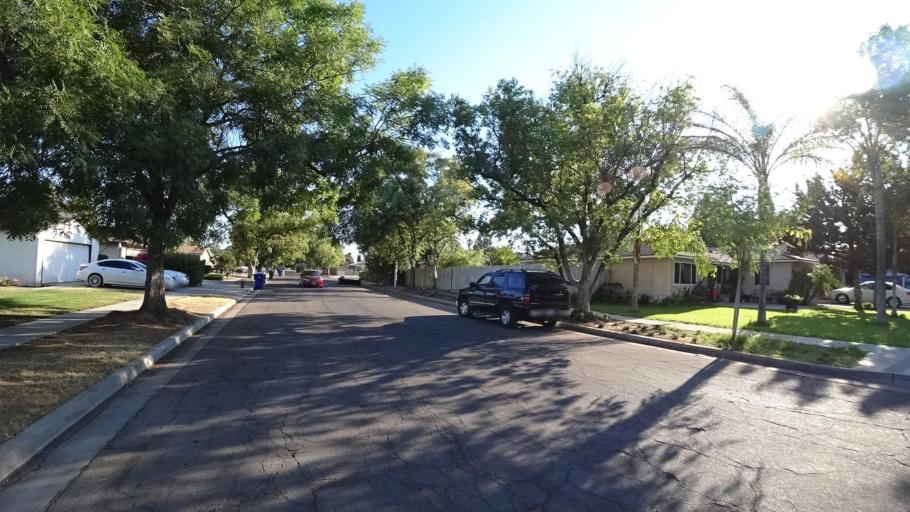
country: US
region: California
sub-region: Fresno County
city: Sunnyside
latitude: 36.7404
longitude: -119.7306
